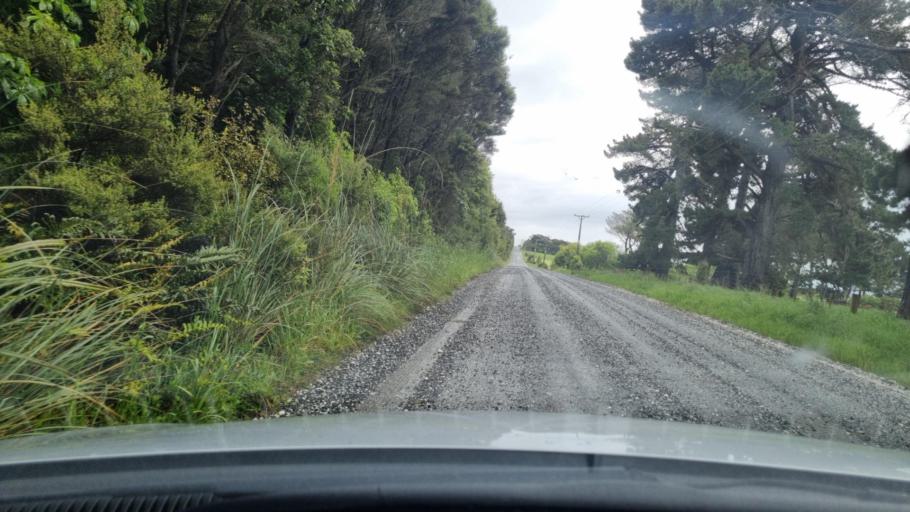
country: NZ
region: Southland
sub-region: Invercargill City
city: Bluff
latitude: -46.5333
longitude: 168.2669
